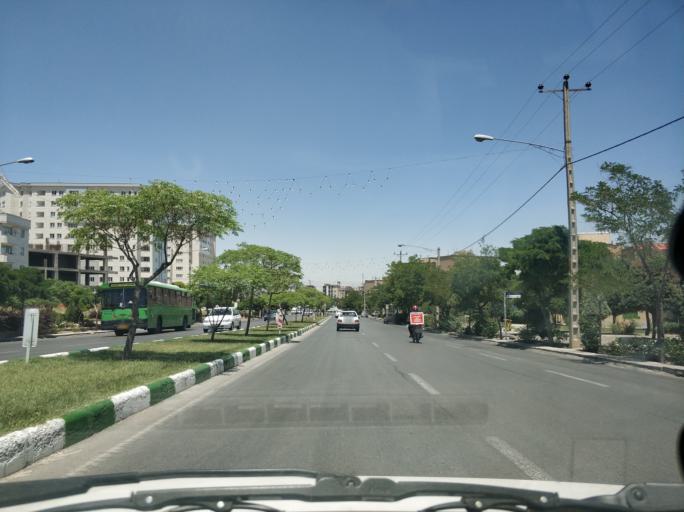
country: IR
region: Razavi Khorasan
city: Mashhad
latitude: 36.2979
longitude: 59.5089
